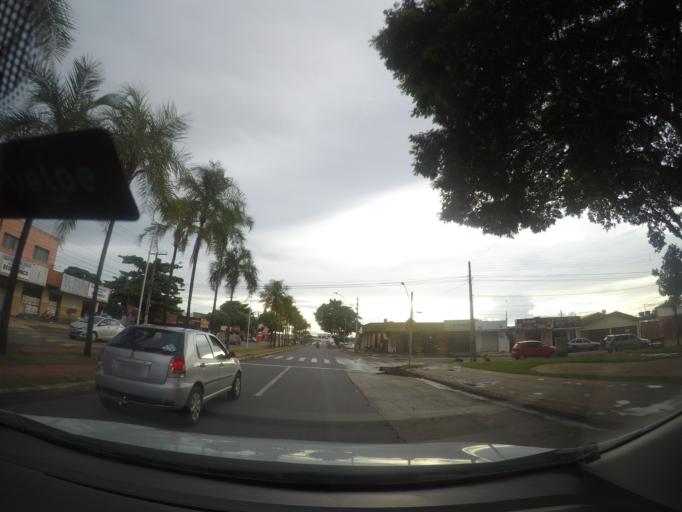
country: BR
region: Goias
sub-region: Goiania
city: Goiania
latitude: -16.7089
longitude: -49.3084
